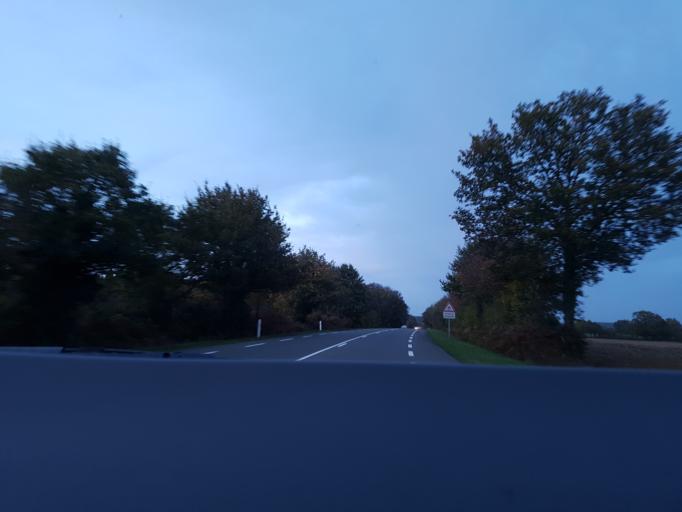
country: FR
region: Pays de la Loire
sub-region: Departement de la Mayenne
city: Ahuille
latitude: 47.9982
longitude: -0.8465
